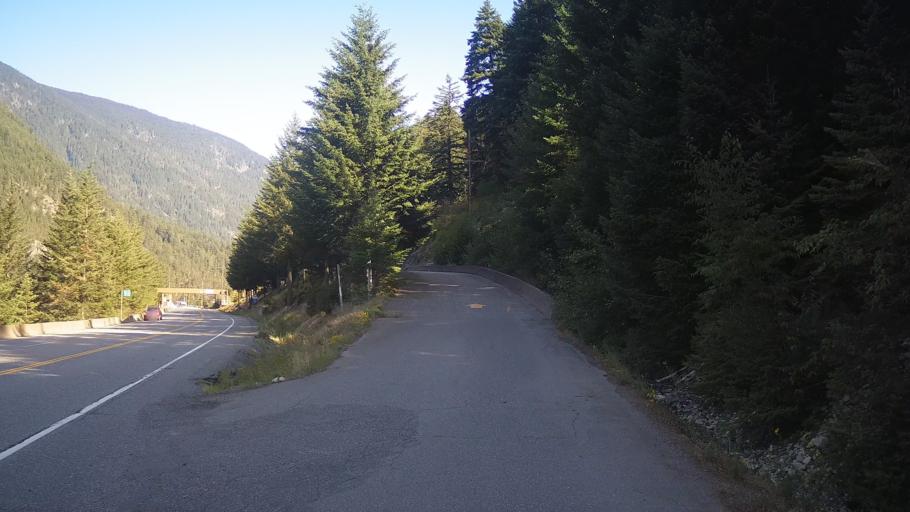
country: CA
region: British Columbia
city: Hope
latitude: 49.7788
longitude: -121.4430
